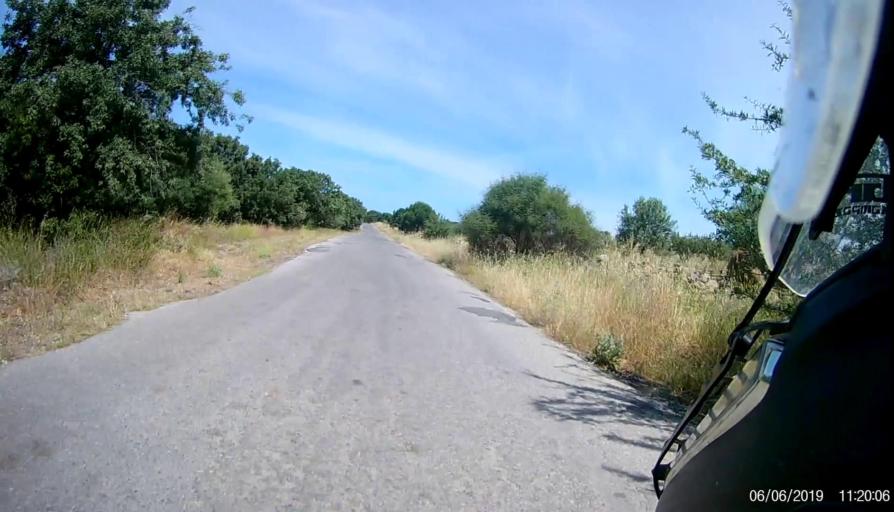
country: TR
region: Canakkale
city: Gulpinar
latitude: 39.6628
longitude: 26.1638
